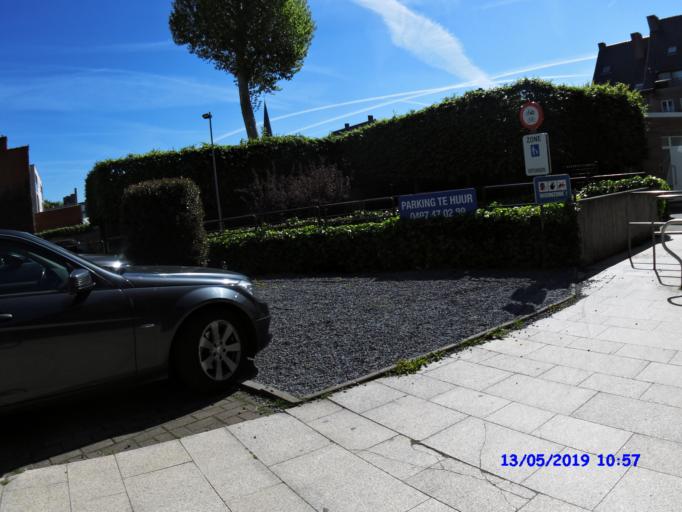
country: BE
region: Flanders
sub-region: Provincie West-Vlaanderen
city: Waregem
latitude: 50.8864
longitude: 3.4294
